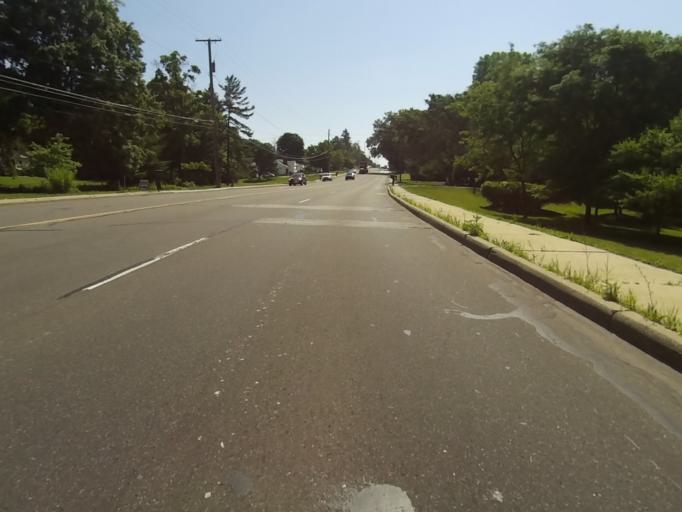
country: US
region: Ohio
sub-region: Summit County
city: Silver Lake
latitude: 41.1666
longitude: -81.4576
